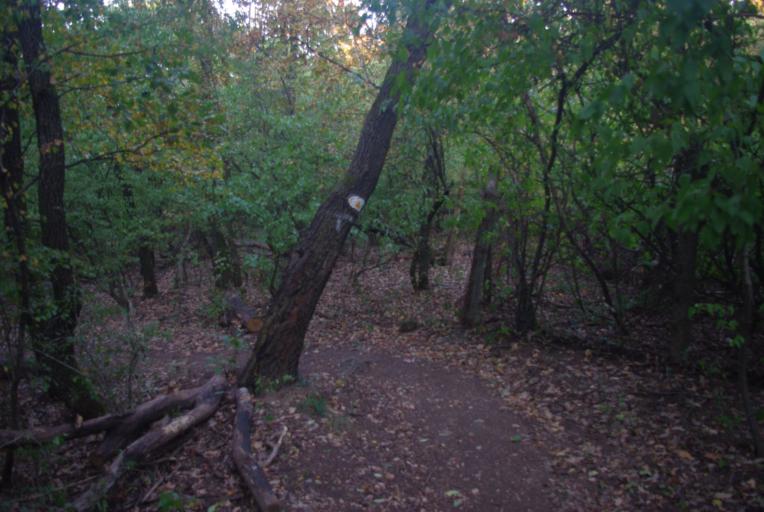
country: HU
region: Heves
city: Gyongyossolymos
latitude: 47.8285
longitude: 19.9631
